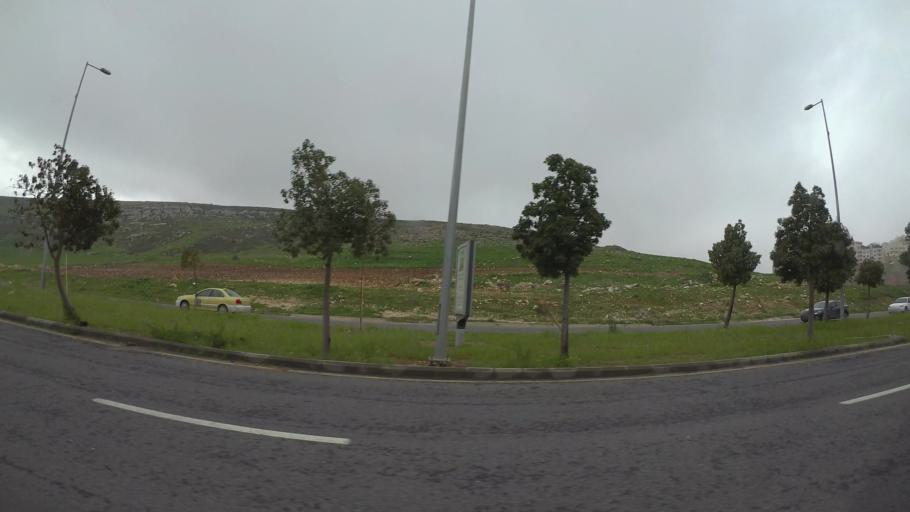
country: JO
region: Amman
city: Al Bunayyat ash Shamaliyah
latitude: 31.9337
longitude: 35.8752
